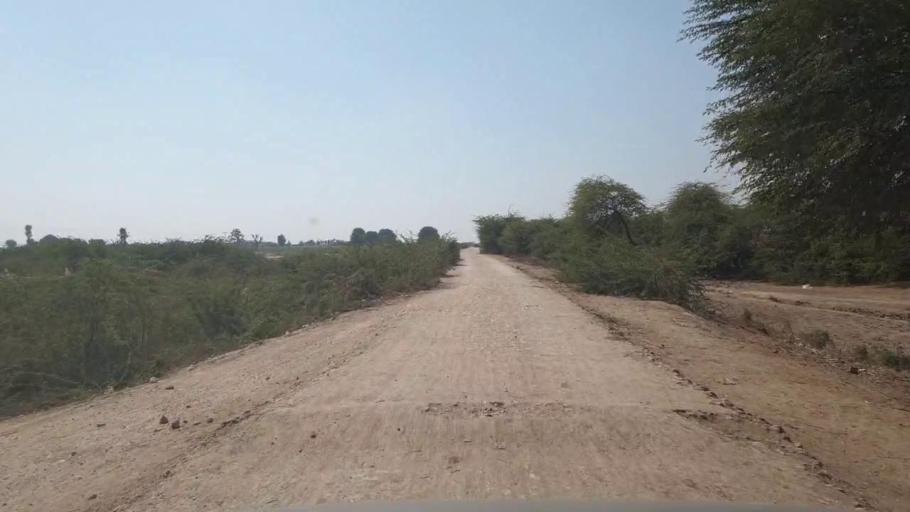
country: PK
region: Sindh
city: Digri
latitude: 25.2403
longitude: 69.2261
